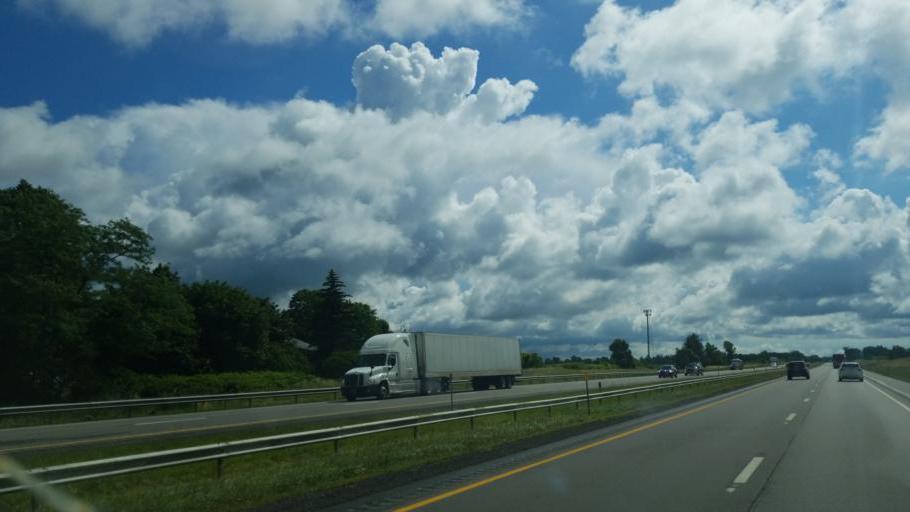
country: US
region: New York
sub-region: Chautauqua County
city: Silver Creek
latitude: 42.5124
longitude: -79.1859
